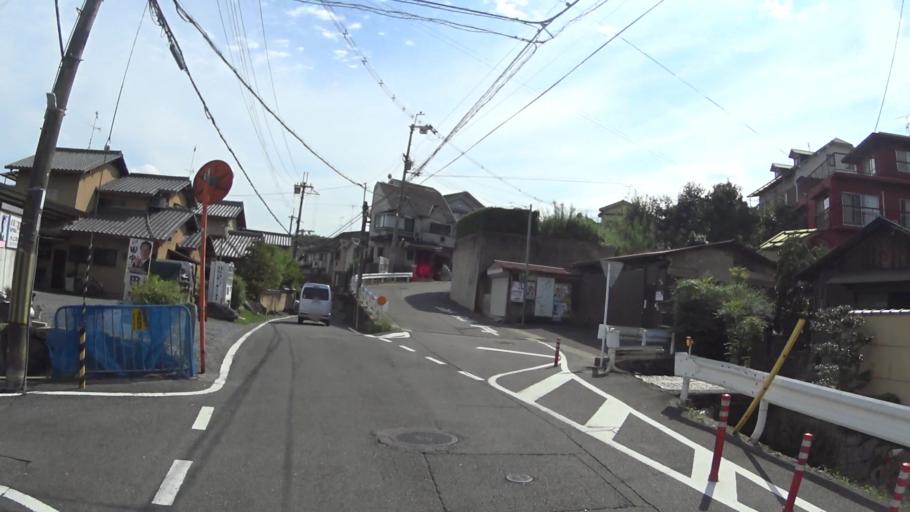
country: JP
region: Kyoto
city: Muko
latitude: 34.9857
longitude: 135.6877
